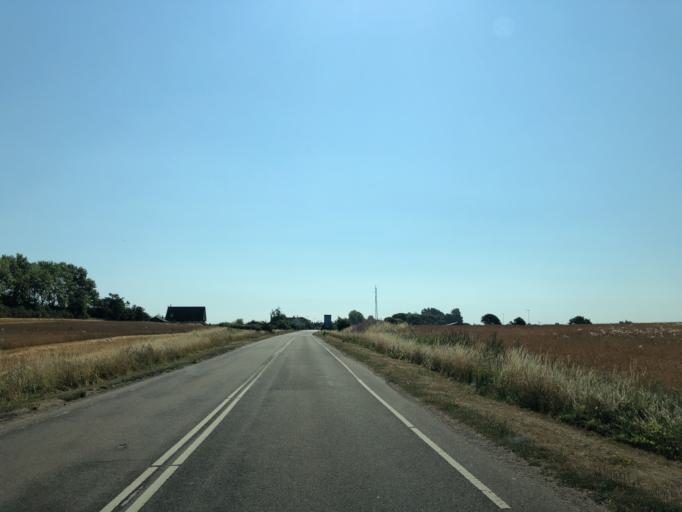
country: DK
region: Zealand
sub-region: Odsherred Kommune
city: Asnaes
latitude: 55.9732
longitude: 11.3519
